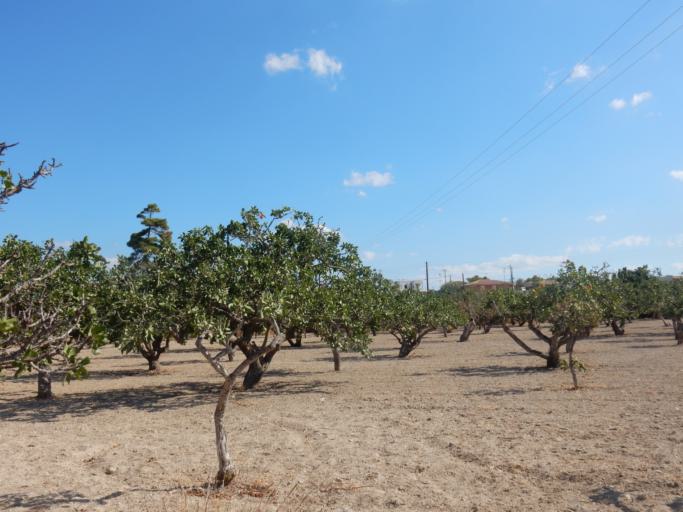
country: GR
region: Attica
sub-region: Nomos Piraios
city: Aegina
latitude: 37.7401
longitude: 23.4359
